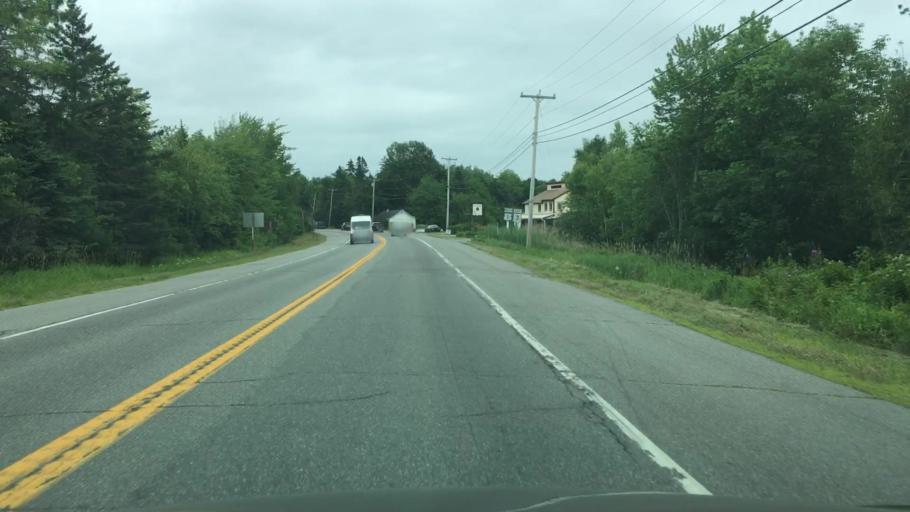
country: US
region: Maine
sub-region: Waldo County
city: Stockton Springs
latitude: 44.4932
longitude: -68.8483
